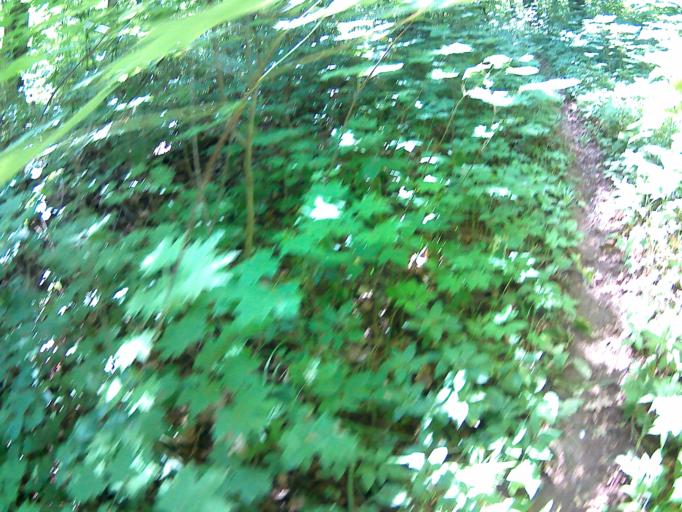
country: RU
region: Nizjnij Novgorod
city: Nizhniy Novgorod
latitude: 56.2294
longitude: 43.9248
